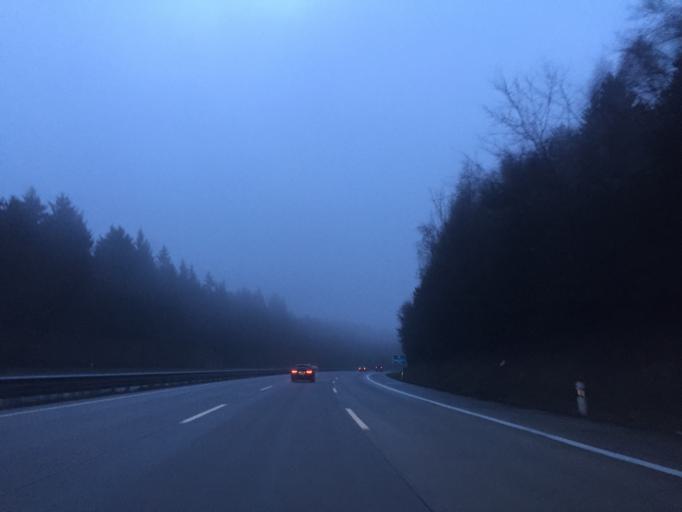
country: DE
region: Rheinland-Pfalz
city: Oberhaid
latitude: 50.5036
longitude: 7.7277
